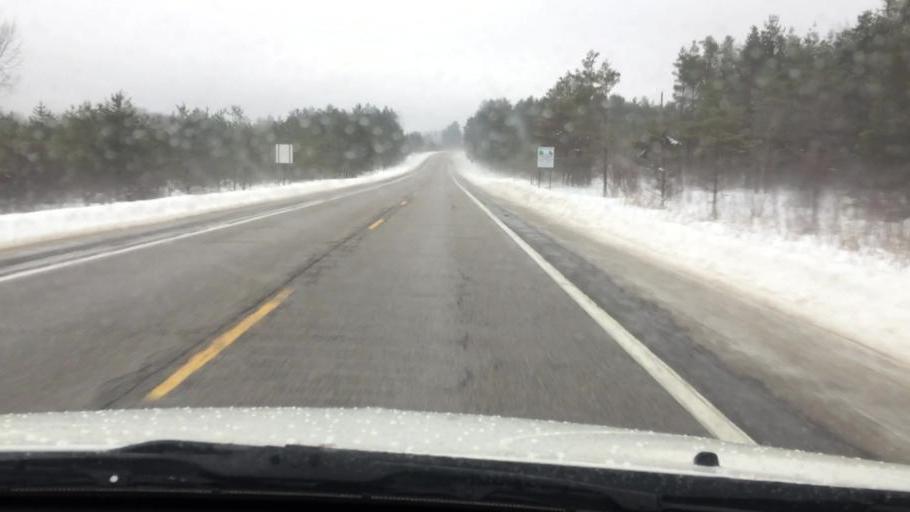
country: US
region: Michigan
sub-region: Charlevoix County
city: East Jordan
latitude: 45.0964
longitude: -85.1047
